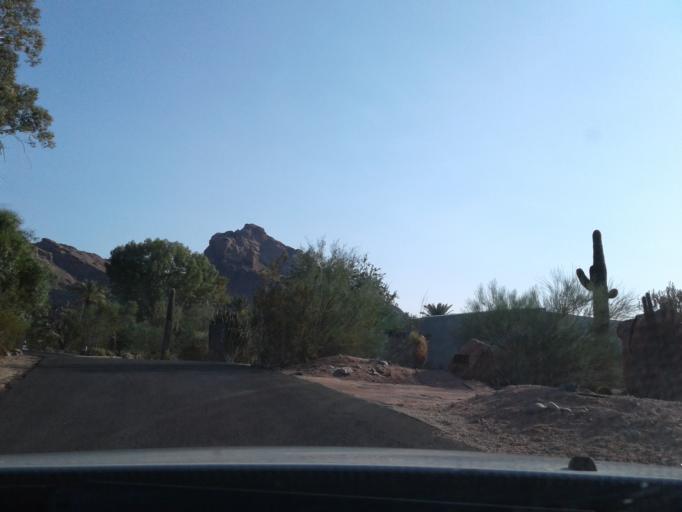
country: US
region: Arizona
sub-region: Maricopa County
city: Paradise Valley
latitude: 33.5296
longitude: -111.9662
